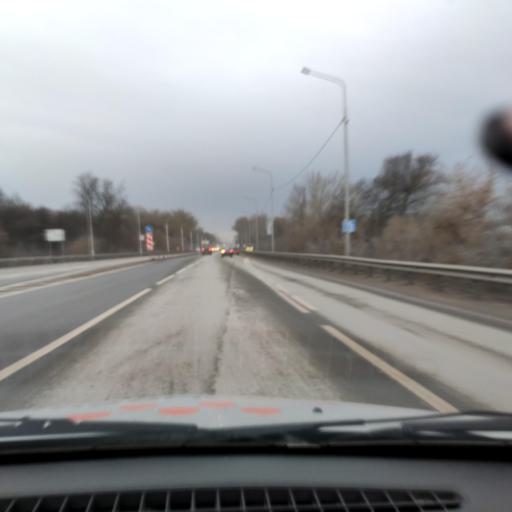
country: RU
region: Bashkortostan
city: Ufa
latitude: 54.7011
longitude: 55.9431
